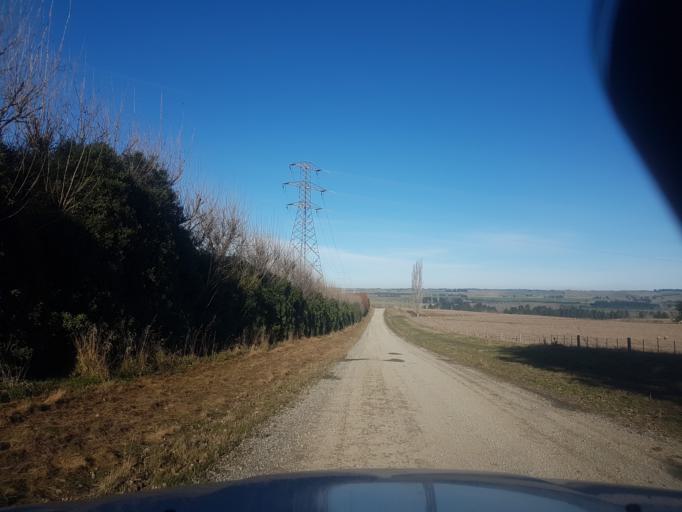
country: NZ
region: Canterbury
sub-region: Timaru District
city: Pleasant Point
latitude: -44.2539
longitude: 171.0434
